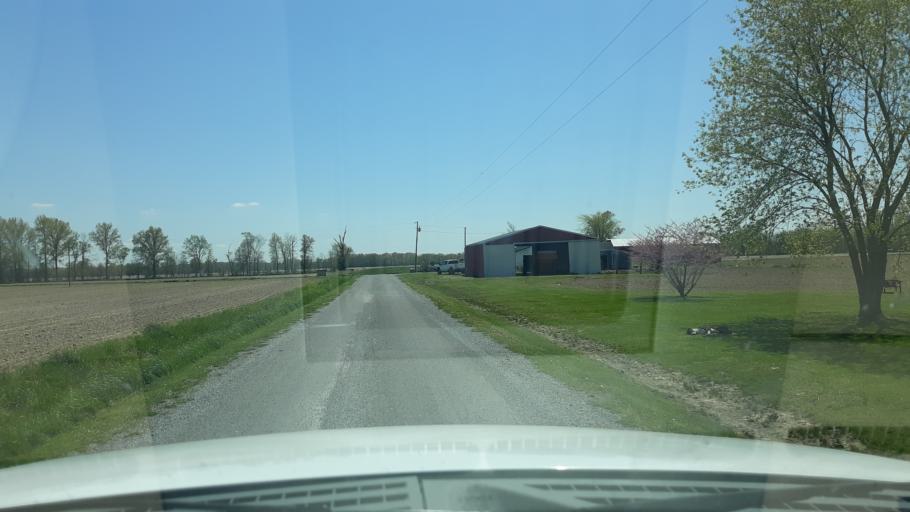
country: US
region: Illinois
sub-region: Saline County
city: Harrisburg
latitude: 37.8914
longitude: -88.6792
